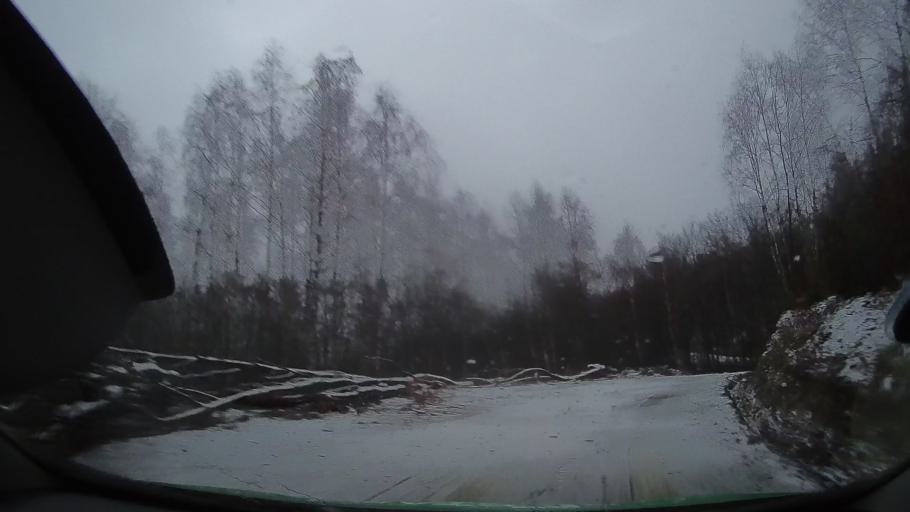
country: RO
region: Alba
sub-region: Comuna Avram Iancu
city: Avram Iancu
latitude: 46.3012
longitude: 22.7935
